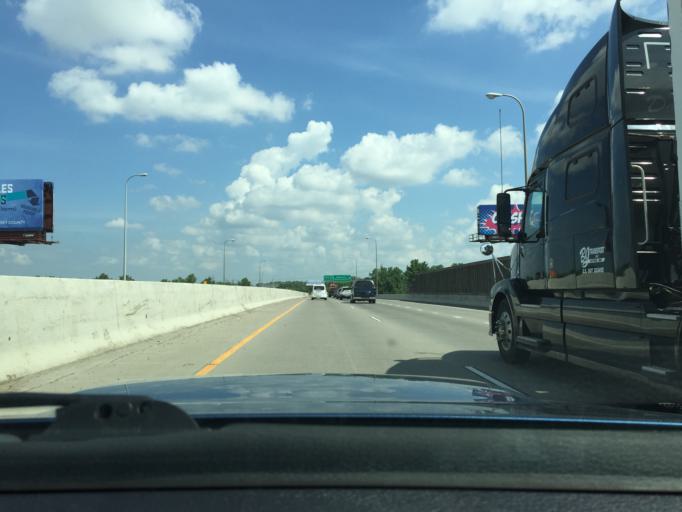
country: US
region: Minnesota
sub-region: Ramsey County
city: Lauderdale
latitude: 44.9727
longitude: -93.2023
